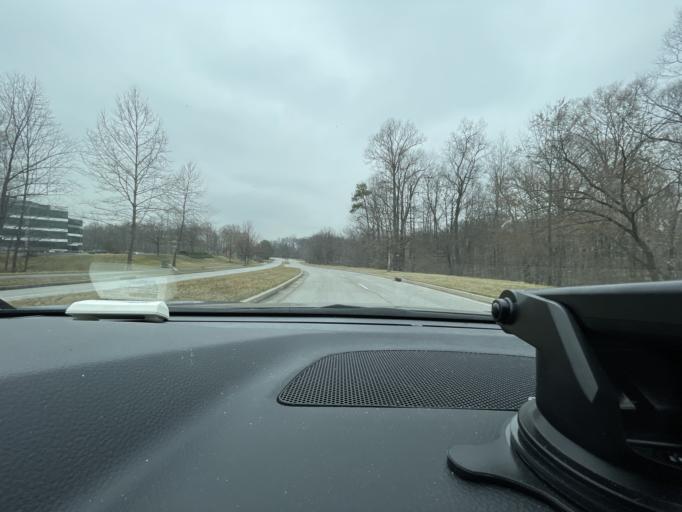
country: US
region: Maryland
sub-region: Anne Arundel County
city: Jessup
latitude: 39.1793
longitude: -76.7991
